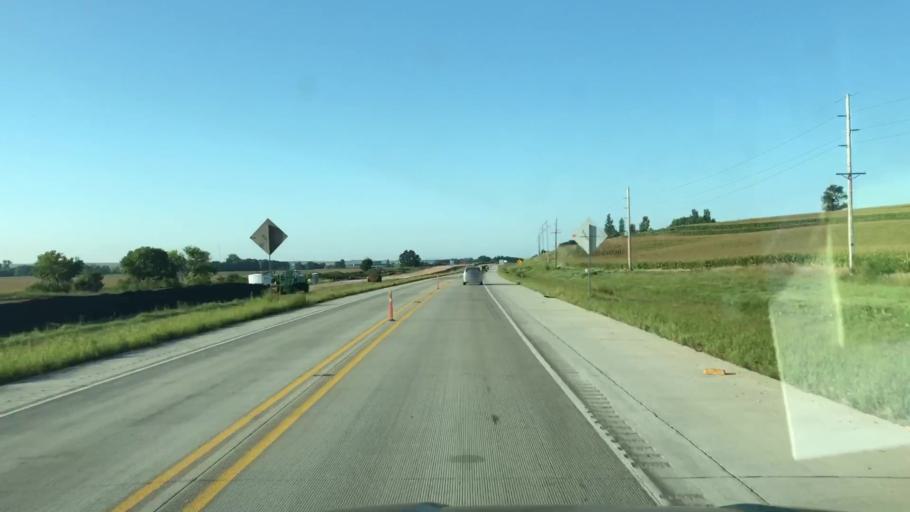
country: US
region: Iowa
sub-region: Plymouth County
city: Le Mars
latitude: 42.7448
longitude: -96.2138
